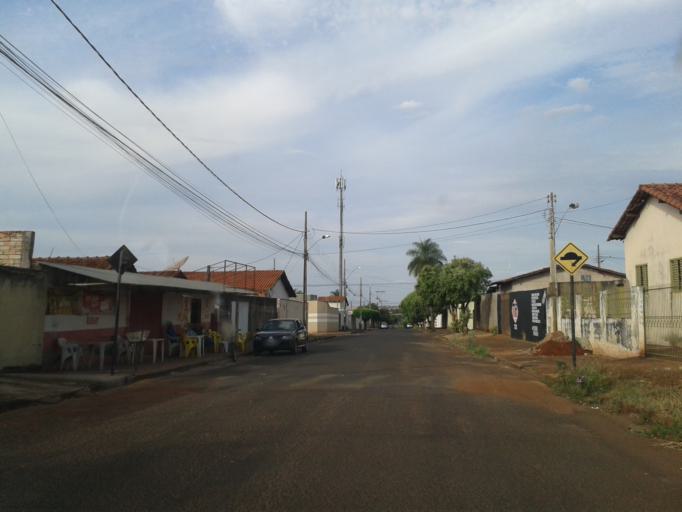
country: BR
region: Minas Gerais
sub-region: Ituiutaba
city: Ituiutaba
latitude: -18.9924
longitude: -49.4523
